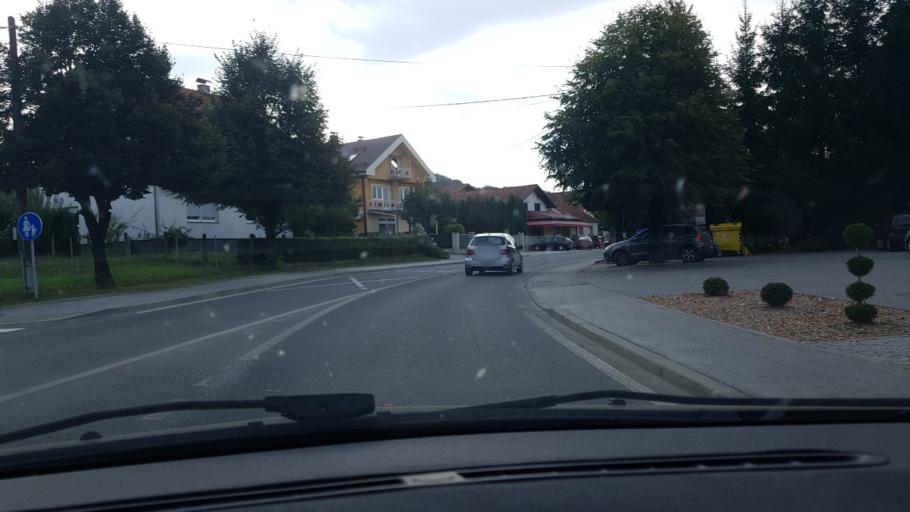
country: HR
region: Krapinsko-Zagorska
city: Zlatar
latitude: 46.0932
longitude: 16.0433
